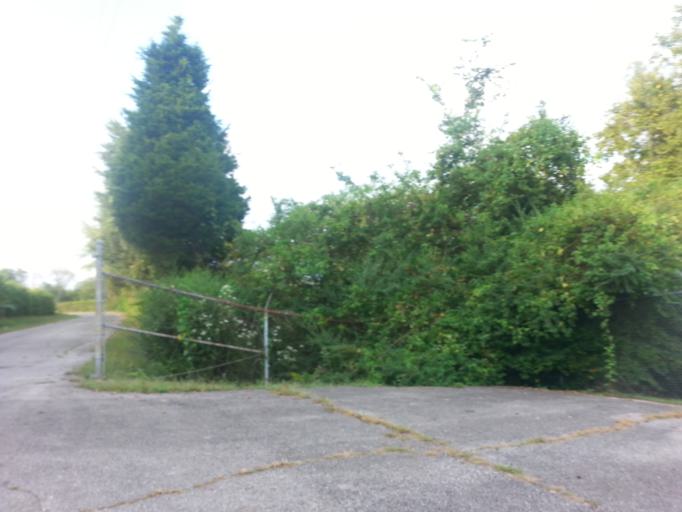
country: US
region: Tennessee
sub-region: Blount County
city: Alcoa
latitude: 35.7960
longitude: -83.9614
